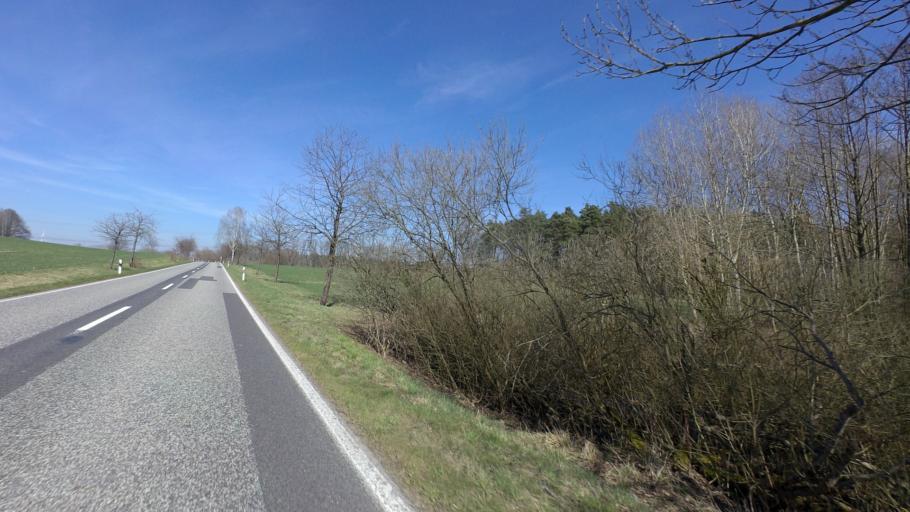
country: DE
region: Brandenburg
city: Furstenwalde
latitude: 52.4168
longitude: 14.0464
